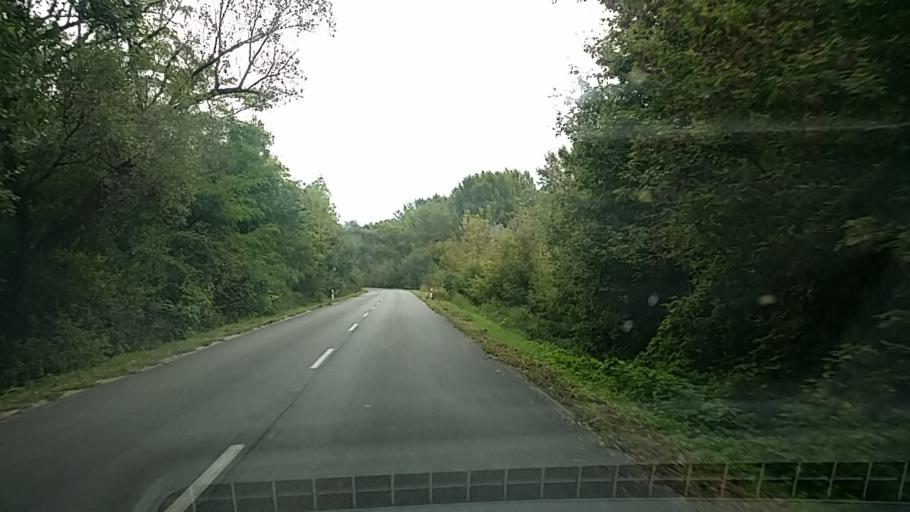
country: HU
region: Komarom-Esztergom
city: Esztergom
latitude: 47.8225
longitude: 18.7593
